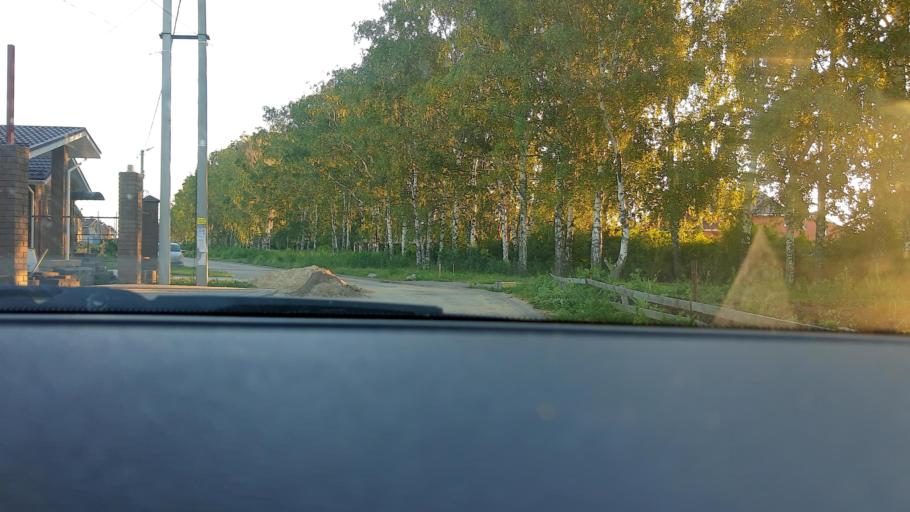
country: RU
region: Nizjnij Novgorod
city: Afonino
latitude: 56.1936
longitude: 44.0816
